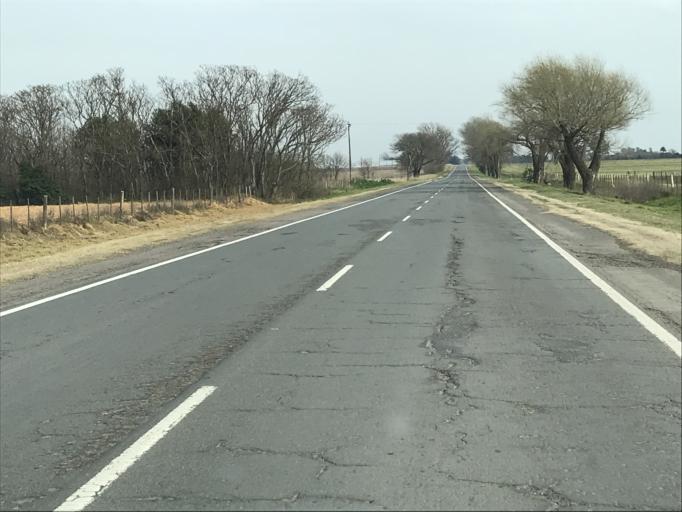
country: AR
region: Santa Fe
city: Armstrong
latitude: -32.7565
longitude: -61.7069
